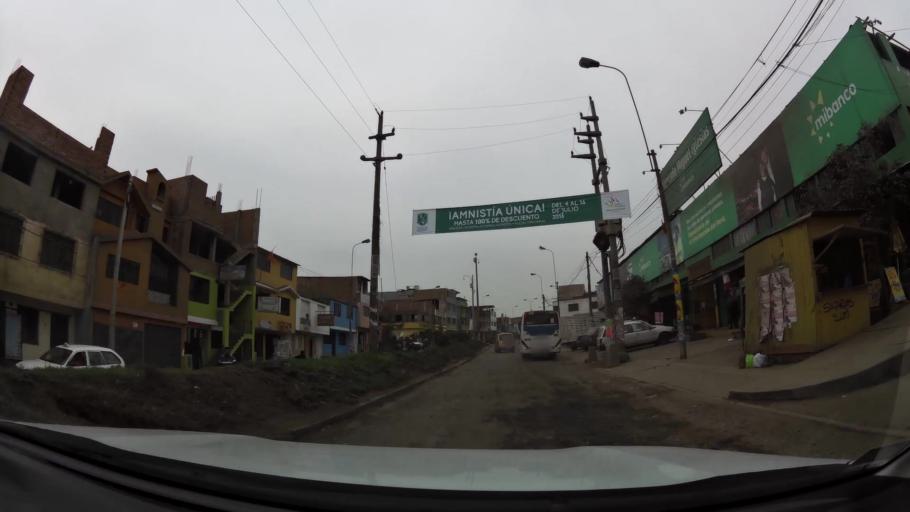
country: PE
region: Lima
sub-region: Lima
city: Surco
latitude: -12.1744
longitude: -76.9625
